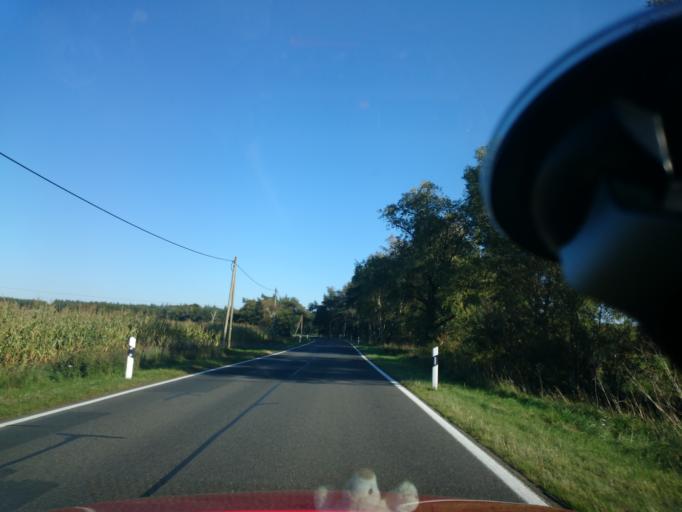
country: DE
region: Mecklenburg-Vorpommern
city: Saal
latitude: 54.3351
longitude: 12.5432
